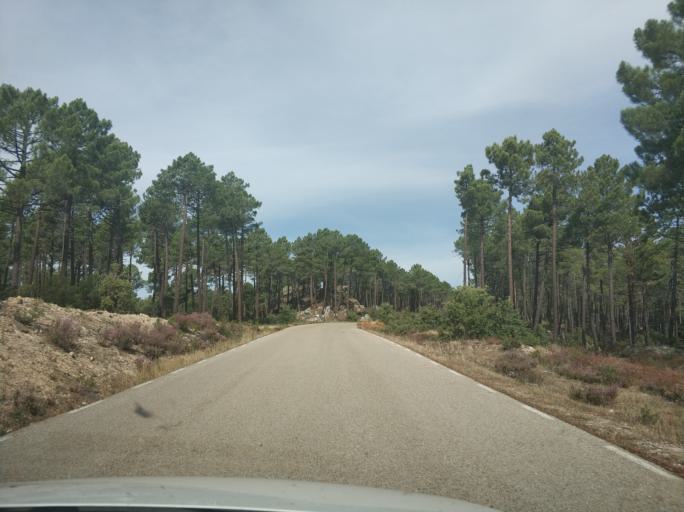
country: ES
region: Castille and Leon
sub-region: Provincia de Soria
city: Duruelo de la Sierra
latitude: 41.8871
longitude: -2.9391
